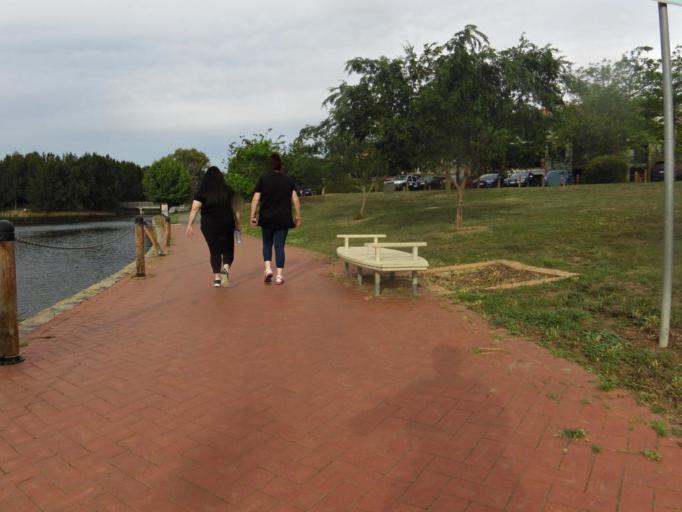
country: AU
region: Australian Capital Territory
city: Kaleen
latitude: -35.1759
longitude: 149.1348
